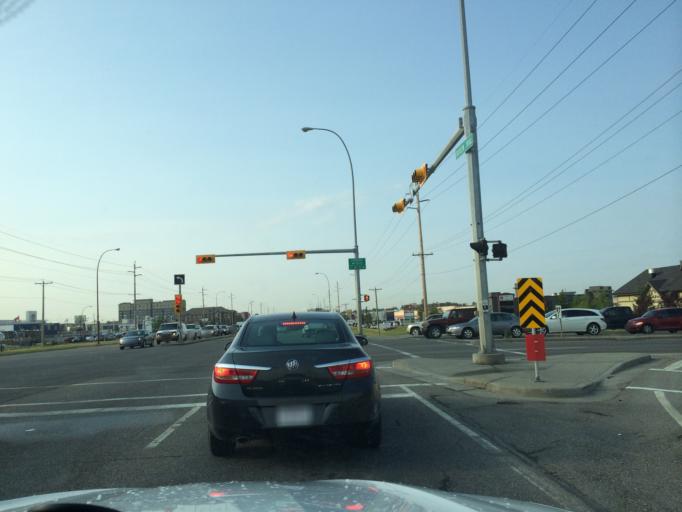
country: CA
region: Alberta
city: Calgary
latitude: 51.0772
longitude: -114.0019
